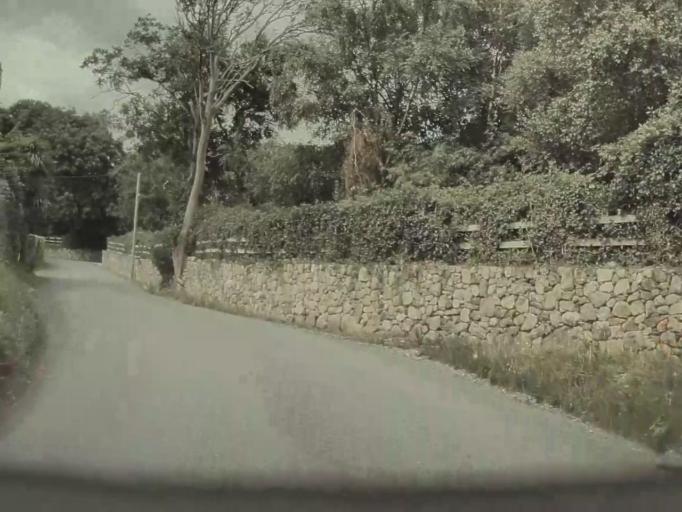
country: IE
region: Leinster
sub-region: Wicklow
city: Kilmacanoge
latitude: 53.1446
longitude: -6.1348
